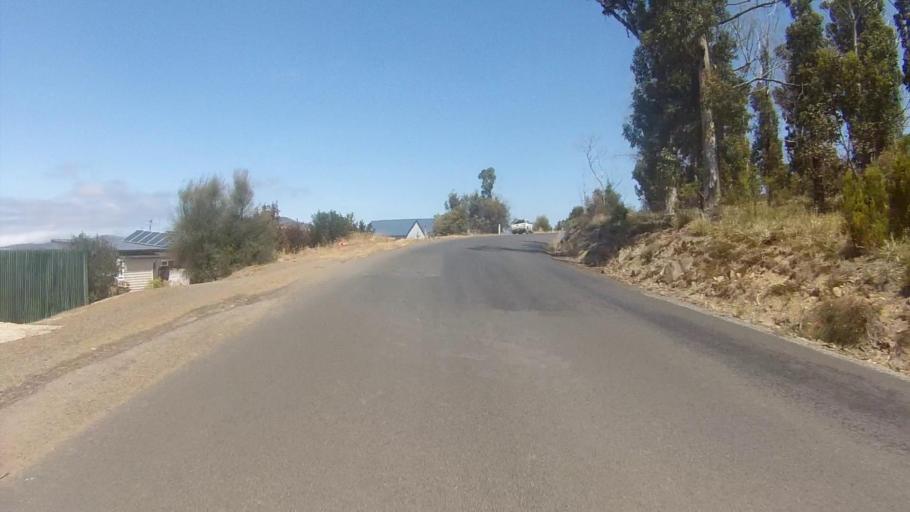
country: AU
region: Tasmania
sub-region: Sorell
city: Sorell
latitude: -42.8721
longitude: 147.8267
